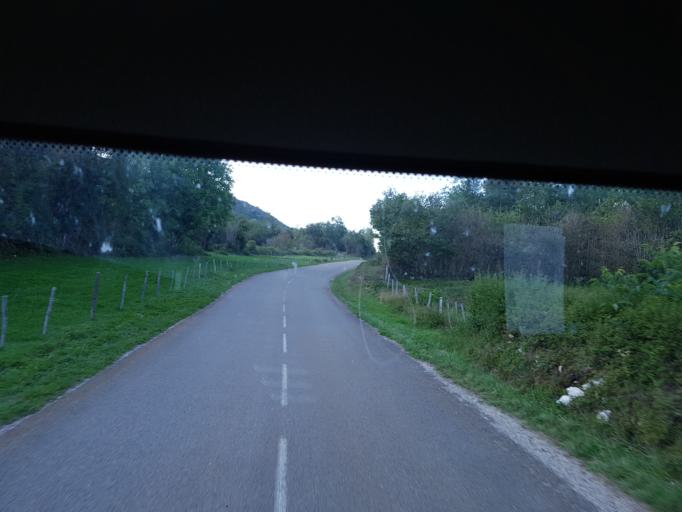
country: FR
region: Franche-Comte
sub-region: Departement du Jura
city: Moirans-en-Montagne
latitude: 46.4086
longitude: 5.6485
